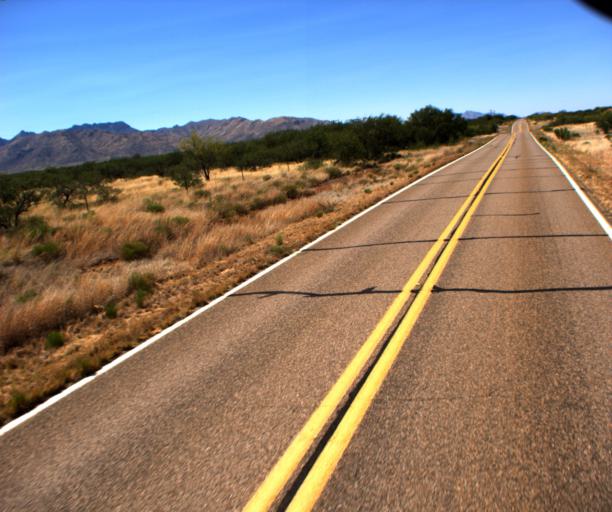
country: US
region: Arizona
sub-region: Pima County
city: Three Points
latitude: 31.6935
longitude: -111.4870
